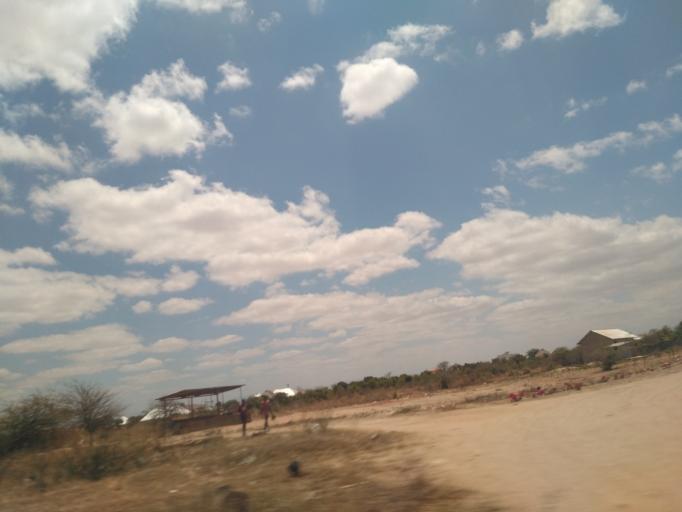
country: TZ
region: Dodoma
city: Kisasa
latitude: -6.1758
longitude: 35.7899
